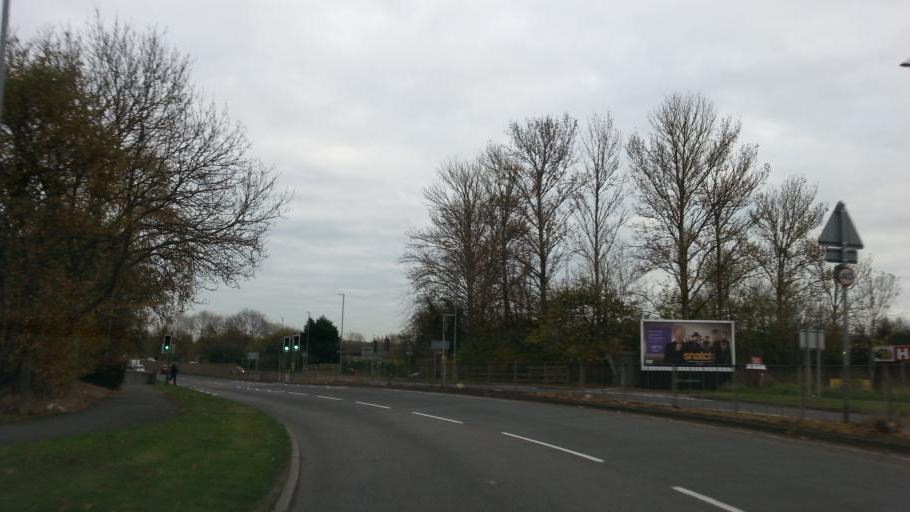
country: GB
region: England
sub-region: Northamptonshire
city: Corby
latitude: 52.4851
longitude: -0.6974
